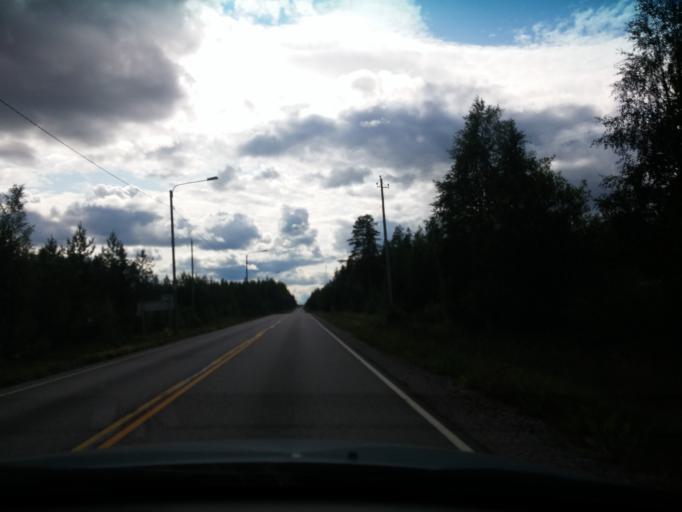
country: FI
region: Central Finland
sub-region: Saarijaervi-Viitasaari
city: Pylkoenmaeki
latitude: 62.6356
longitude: 24.8173
